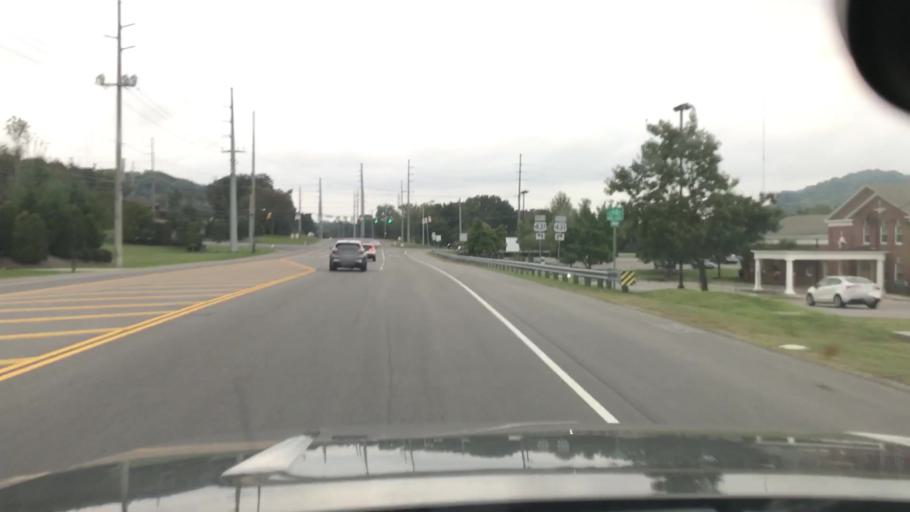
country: US
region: Tennessee
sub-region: Davidson County
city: Forest Hills
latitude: 36.0478
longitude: -86.8648
